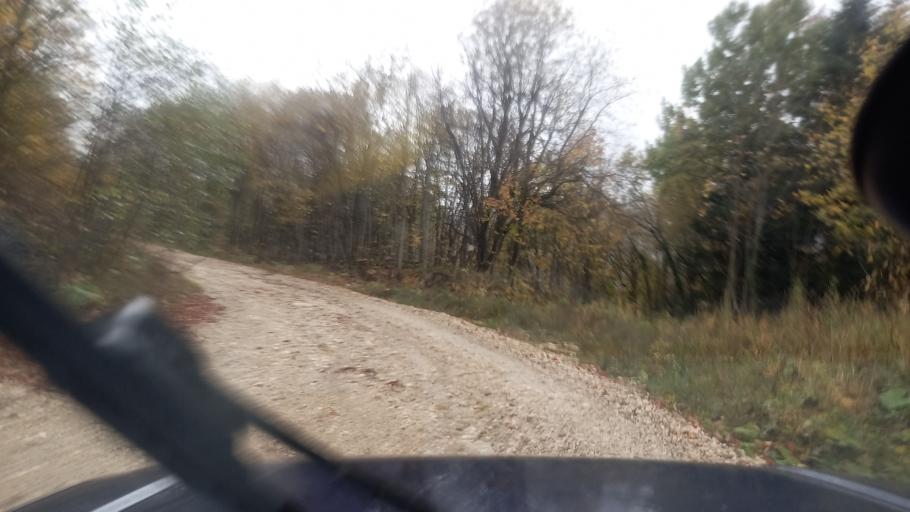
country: RU
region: Krasnodarskiy
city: Neftegorsk
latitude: 44.0243
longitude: 39.8380
